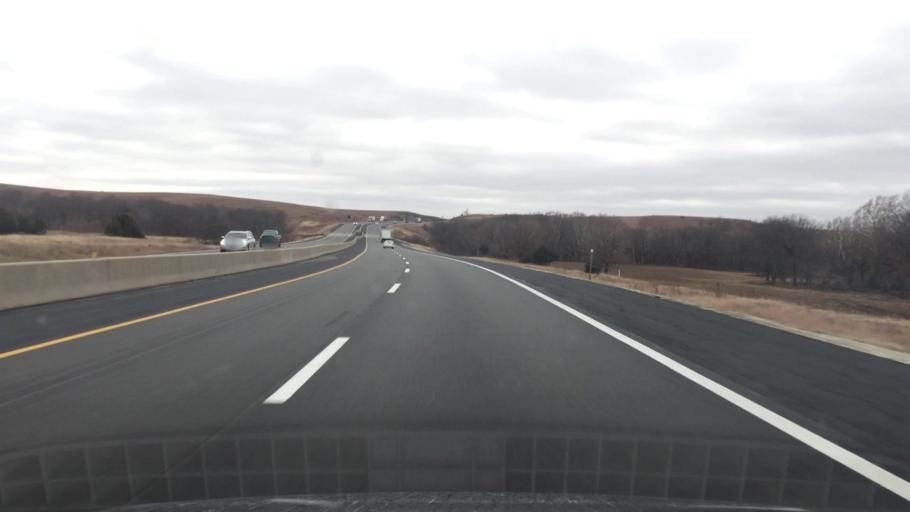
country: US
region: Kansas
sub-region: Chase County
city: Cottonwood Falls
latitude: 38.1413
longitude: -96.5247
